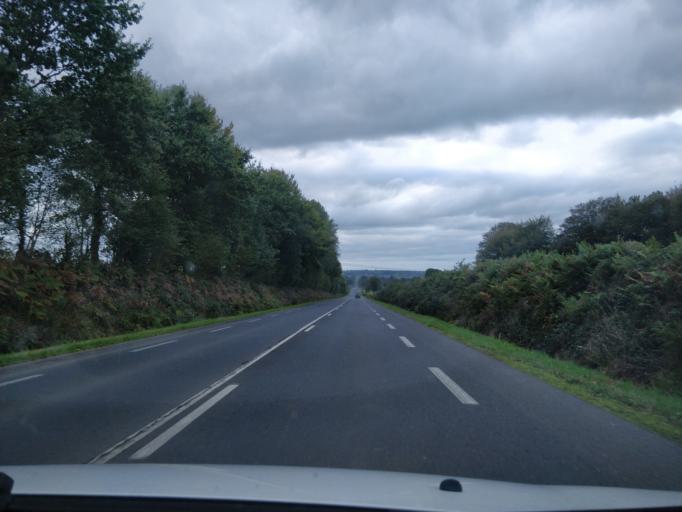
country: FR
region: Lower Normandy
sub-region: Departement de la Manche
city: Villedieu-les-Poeles
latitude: 48.8234
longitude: -1.1340
